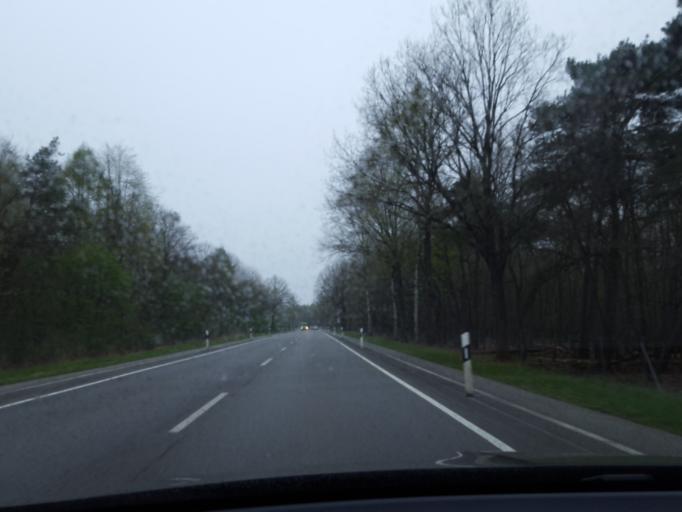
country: DE
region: North Rhine-Westphalia
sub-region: Regierungsbezirk Dusseldorf
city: Schermbeck
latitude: 51.7157
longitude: 6.9243
